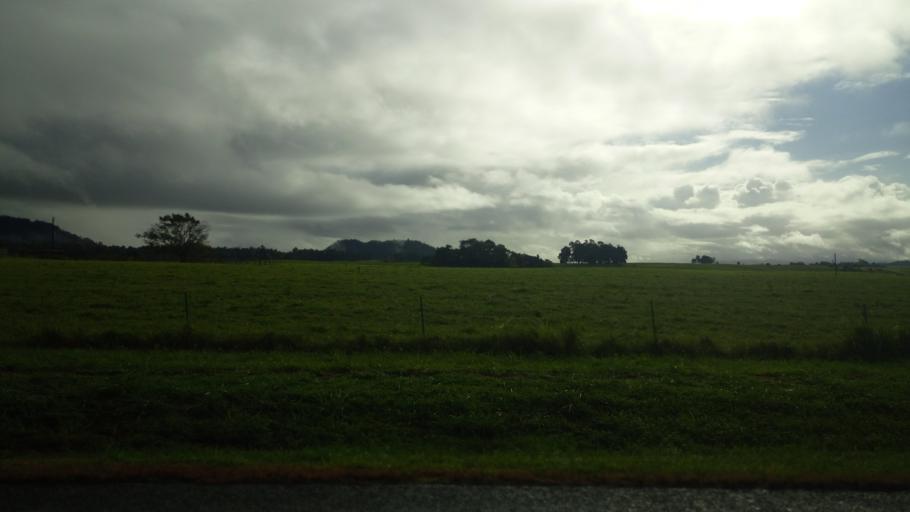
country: AU
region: Queensland
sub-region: Cassowary Coast
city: Innisfail
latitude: -17.6243
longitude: 145.8059
